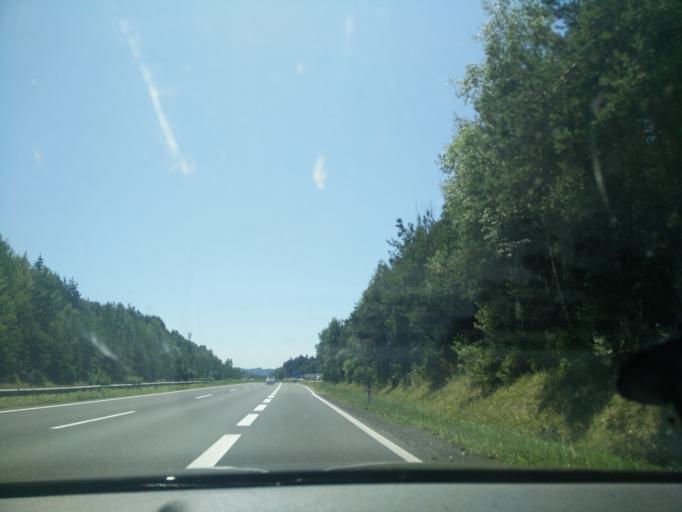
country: AT
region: Styria
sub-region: Politischer Bezirk Hartberg-Fuerstenfeld
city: Hainersdorf
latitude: 47.1223
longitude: 15.9840
